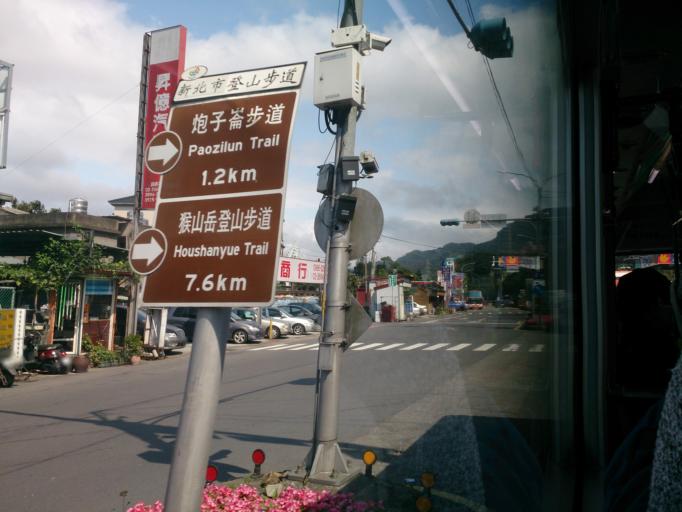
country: TW
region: Taipei
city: Taipei
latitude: 24.9982
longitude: 121.6121
